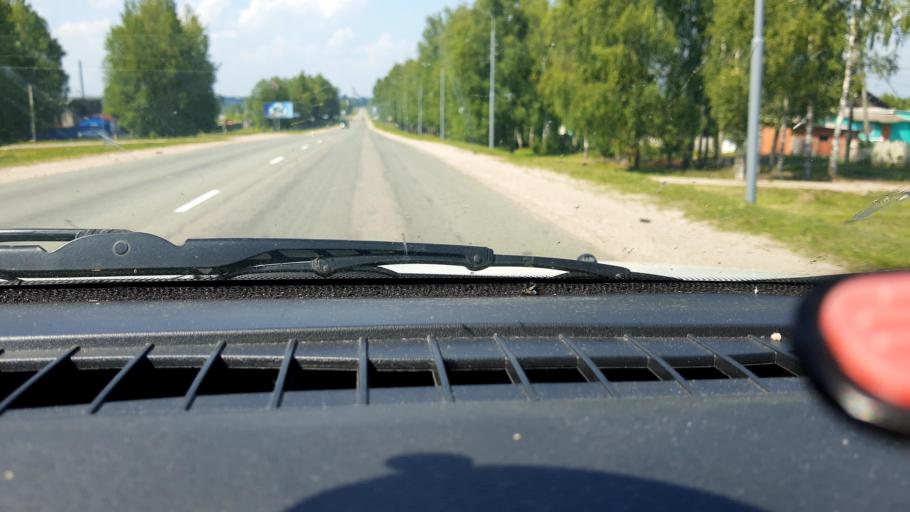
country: RU
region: Nizjnij Novgorod
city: Sharanga
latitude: 57.1878
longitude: 46.5320
